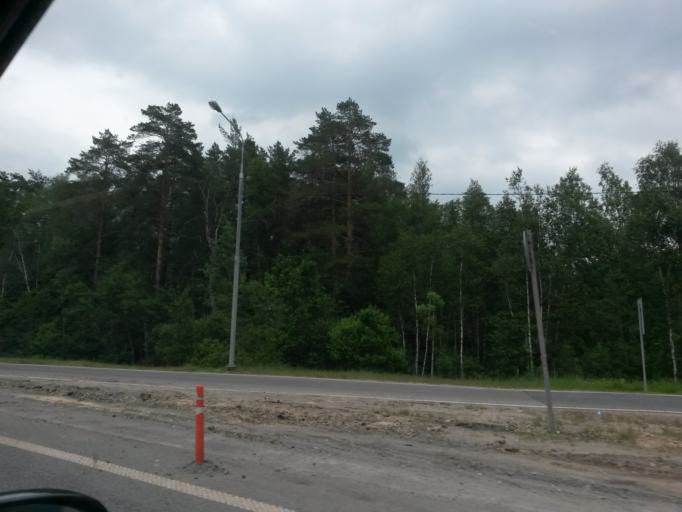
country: RU
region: Moskovskaya
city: Lyubuchany
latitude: 55.1889
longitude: 37.5347
